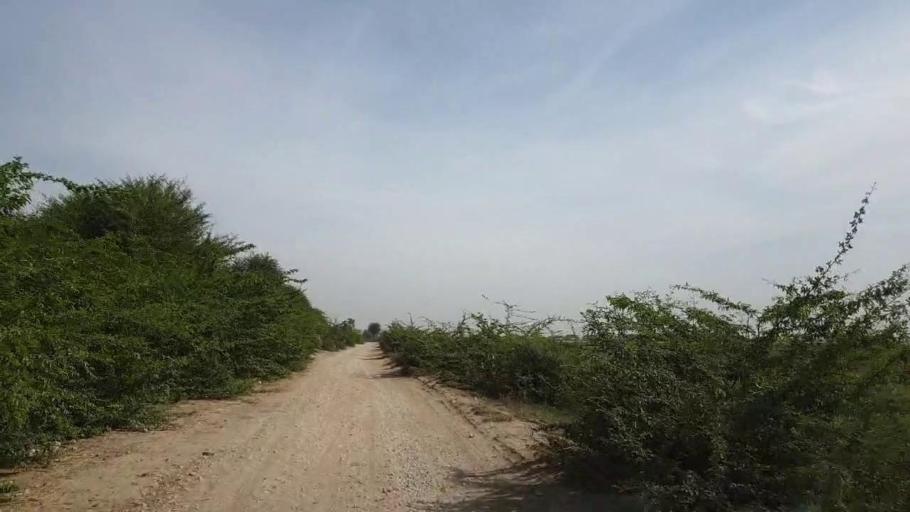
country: PK
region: Sindh
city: Kunri
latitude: 25.1715
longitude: 69.6236
